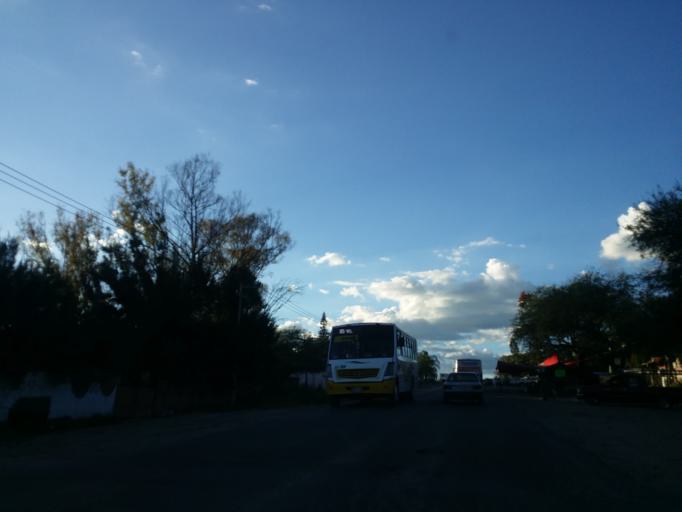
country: MX
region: Guanajuato
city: Leon
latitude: 21.1994
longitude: -101.6716
